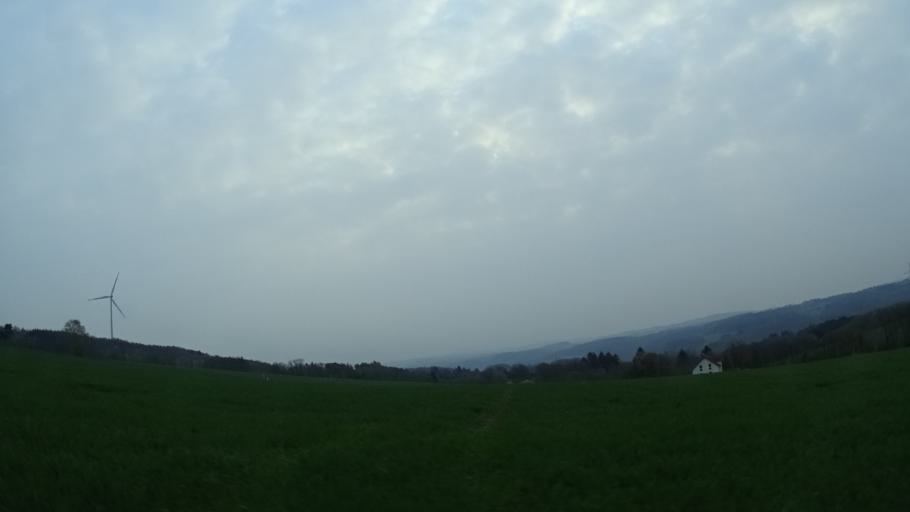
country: DE
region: Rheinland-Pfalz
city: Rimsberg
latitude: 49.6339
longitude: 7.2085
